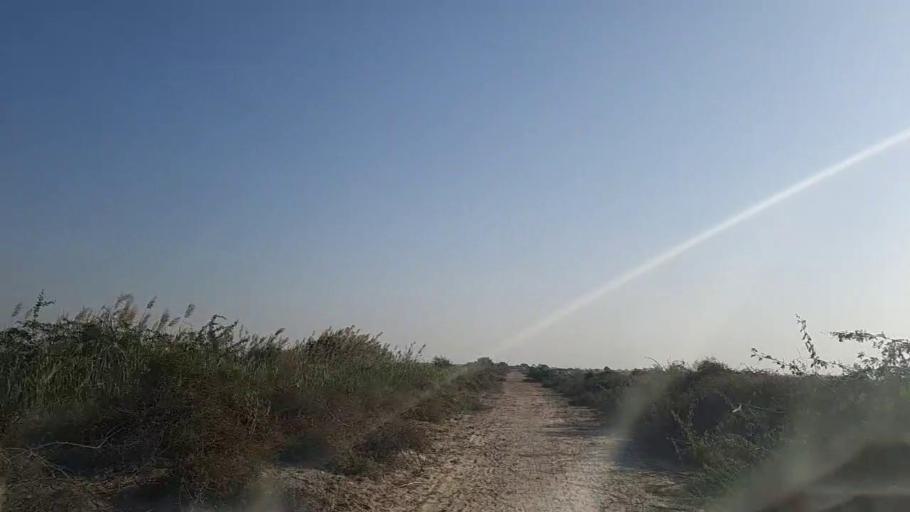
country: PK
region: Sindh
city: Jati
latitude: 24.3935
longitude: 68.2302
